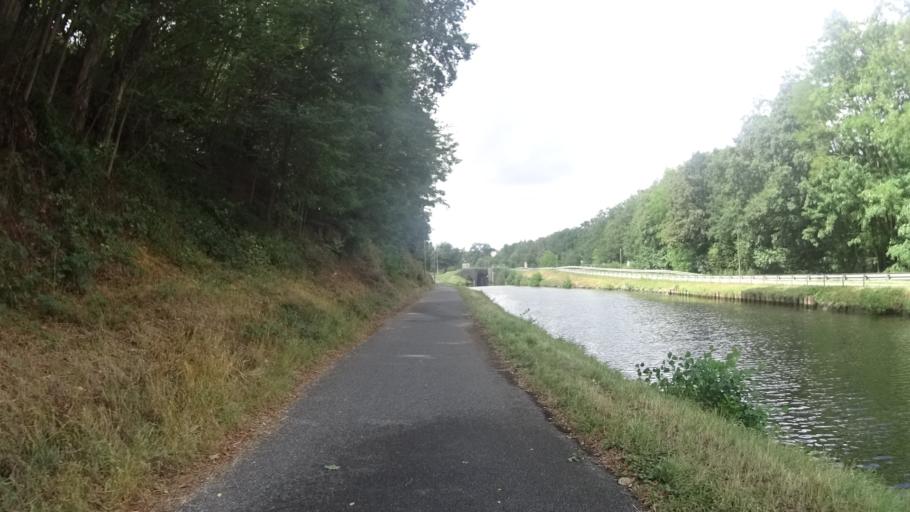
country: FR
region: Bourgogne
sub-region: Departement de Saone-et-Loire
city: Ecuisses
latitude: 46.7798
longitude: 4.5476
